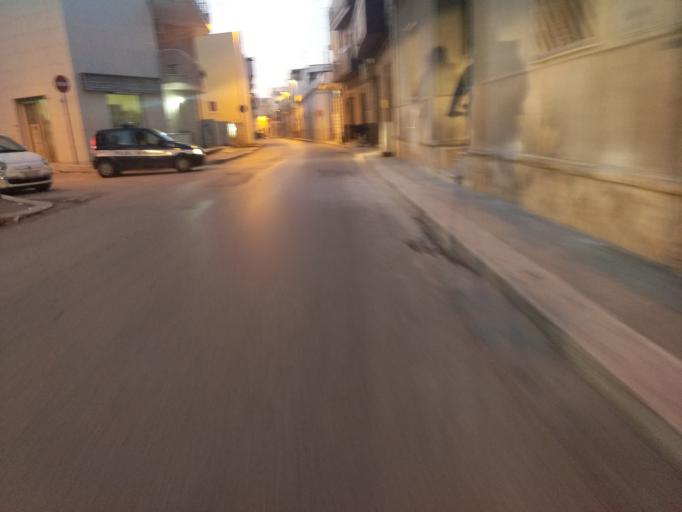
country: IT
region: Apulia
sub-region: Provincia di Bari
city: Modugno
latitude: 41.0792
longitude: 16.7808
